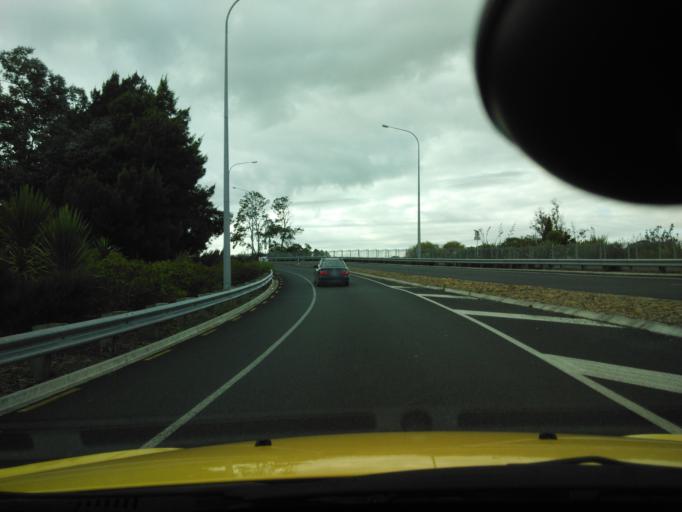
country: NZ
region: Waikato
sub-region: Waikato District
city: Ngaruawahia
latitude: -37.6120
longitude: 175.1874
